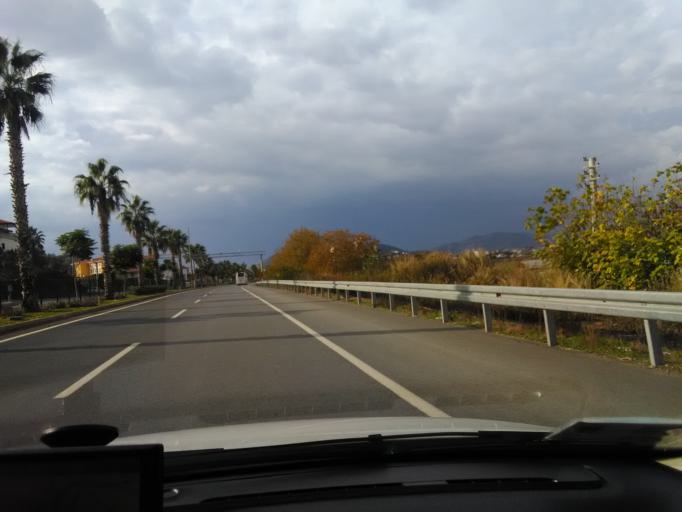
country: TR
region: Antalya
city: Gazipasa
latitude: 36.2558
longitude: 32.3305
